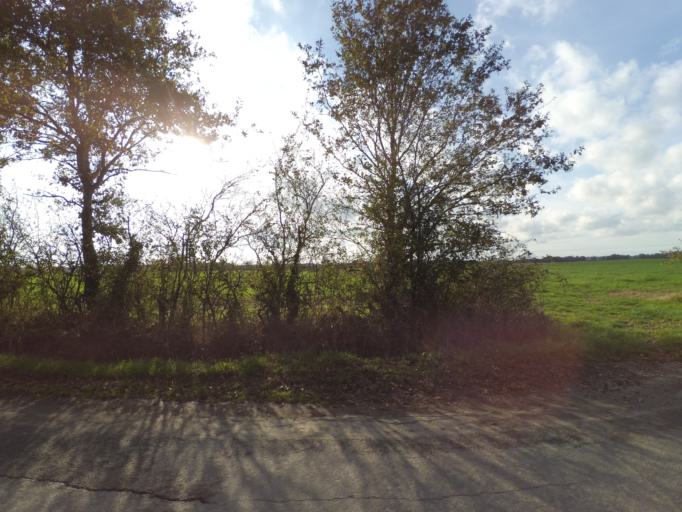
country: FR
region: Pays de la Loire
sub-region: Departement de la Vendee
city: Saint-Hilaire-de-Loulay
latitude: 47.0209
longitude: -1.3564
